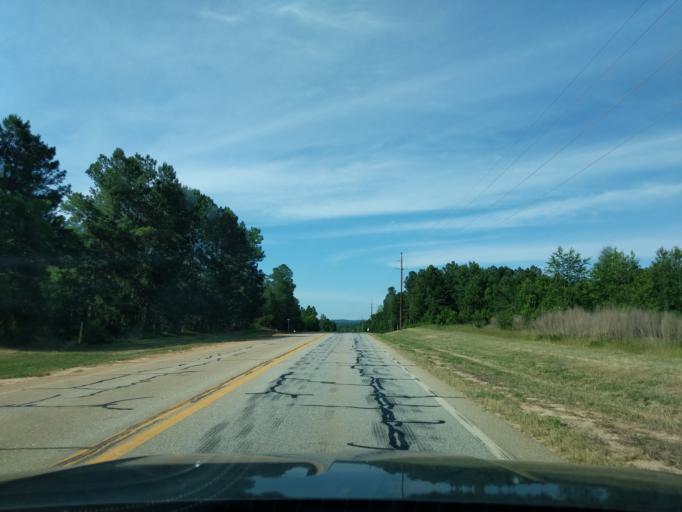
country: US
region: Georgia
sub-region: Jefferson County
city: Wrens
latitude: 33.2878
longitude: -82.3814
